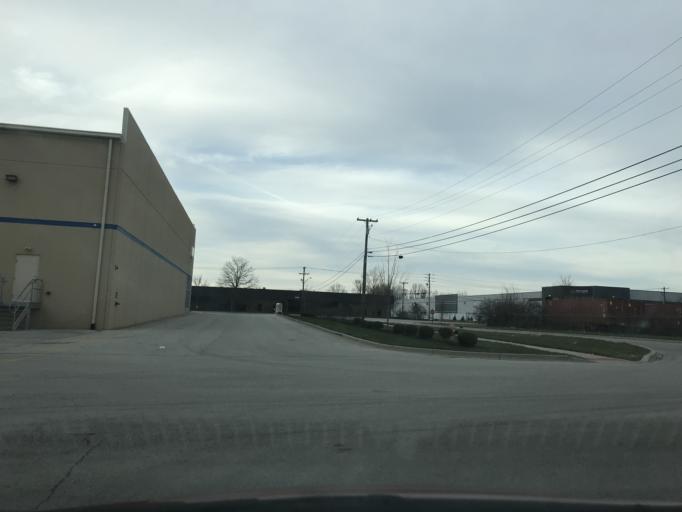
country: US
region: Kentucky
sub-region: Jefferson County
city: West Buechel
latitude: 38.1852
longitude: -85.6791
